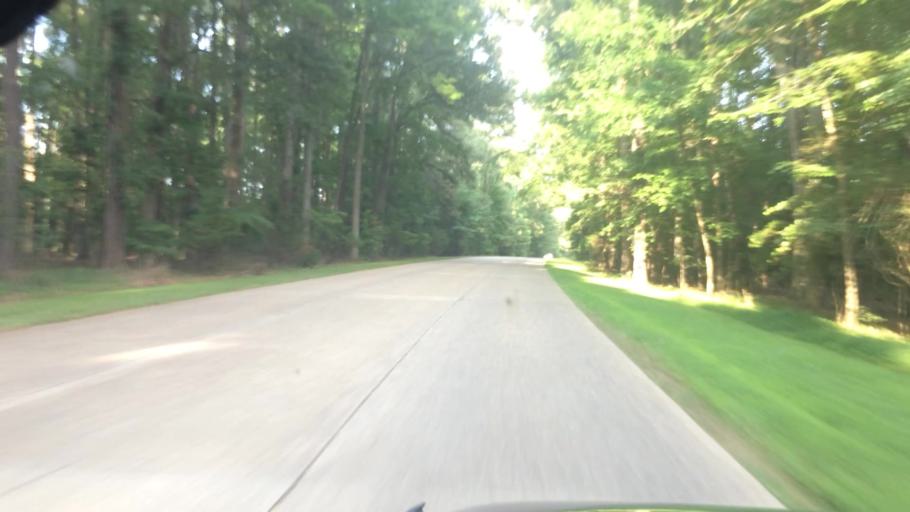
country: US
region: Virginia
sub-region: James City County
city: Williamsburg
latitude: 37.2167
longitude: -76.7519
